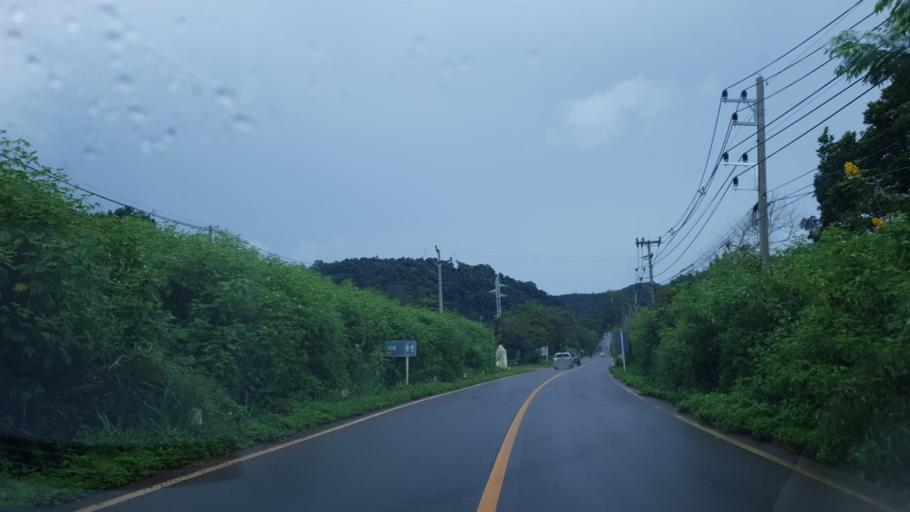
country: TH
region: Mae Hong Son
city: Pa Pae
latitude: 18.1675
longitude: 98.0661
